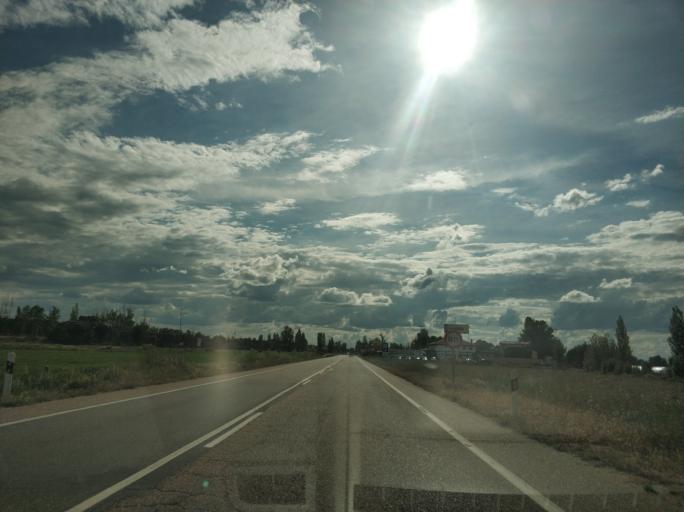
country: ES
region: Castille and Leon
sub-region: Provincia de Burgos
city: Villalba de Duero
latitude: 41.6632
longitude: -3.7394
